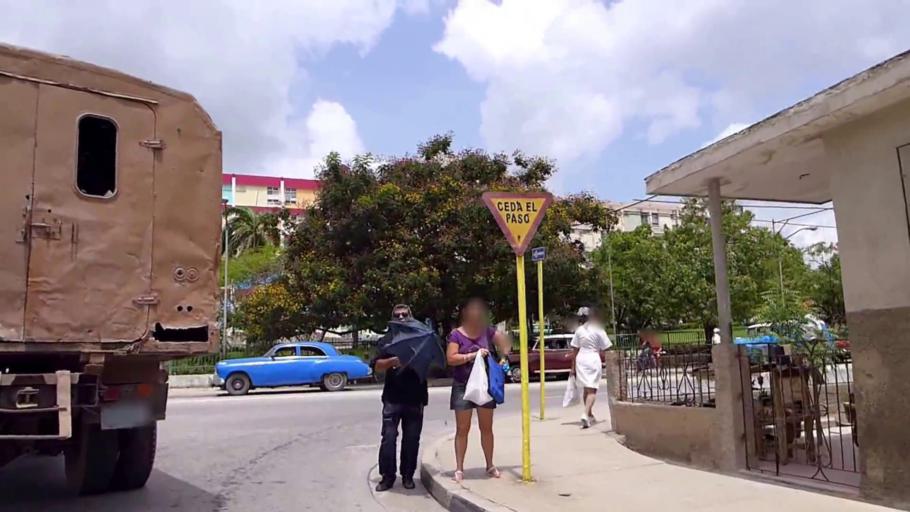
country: CU
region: Holguin
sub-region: Municipio de Holguin
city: Holguin
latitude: 20.8882
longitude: -76.2678
